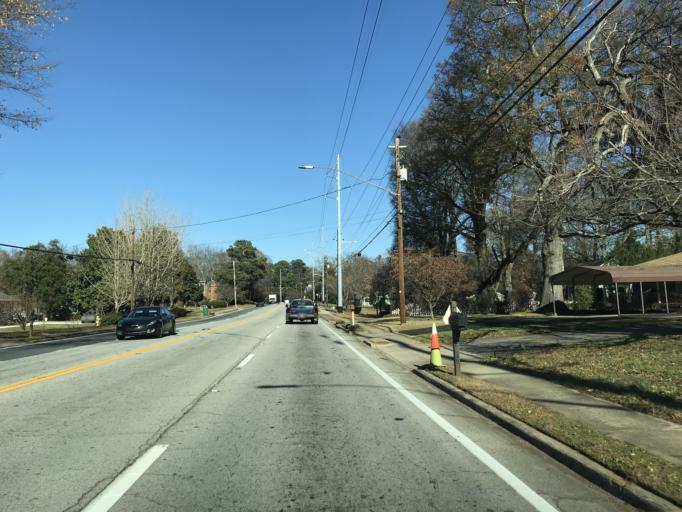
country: US
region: Georgia
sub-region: DeKalb County
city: Tucker
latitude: 33.8624
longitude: -84.2187
